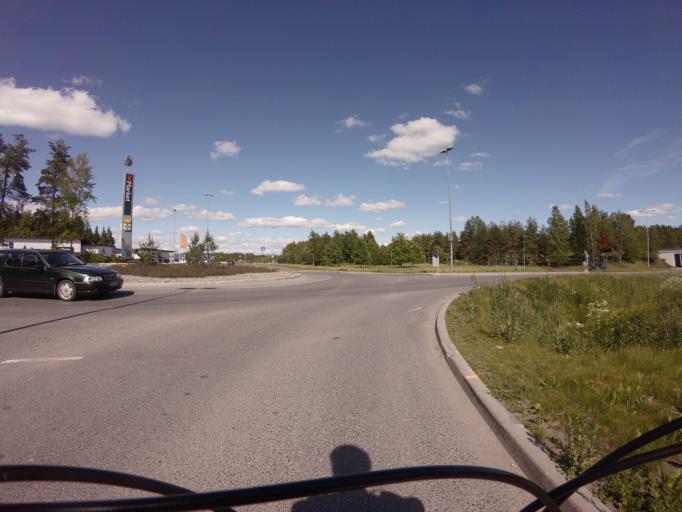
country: FI
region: Varsinais-Suomi
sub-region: Turku
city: Vahto
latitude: 60.5340
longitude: 22.3060
